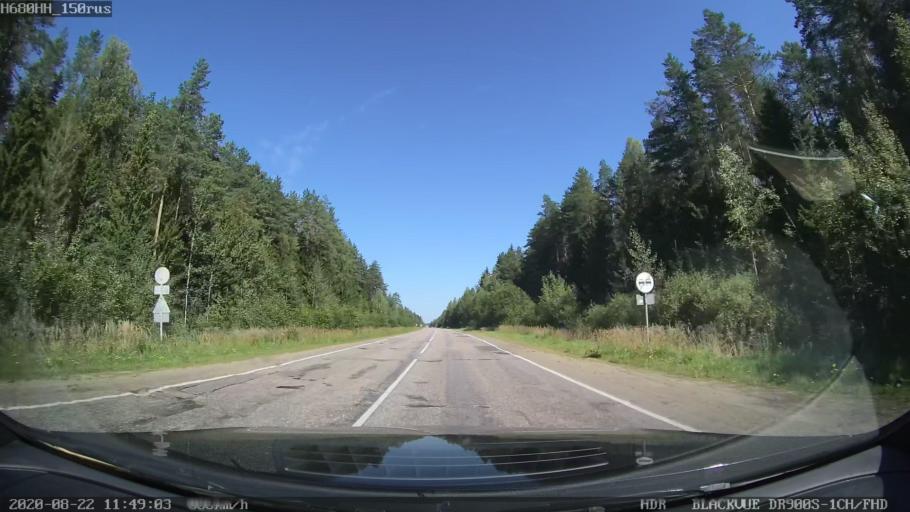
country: RU
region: Tverskaya
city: Sakharovo
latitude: 57.0707
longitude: 36.1099
